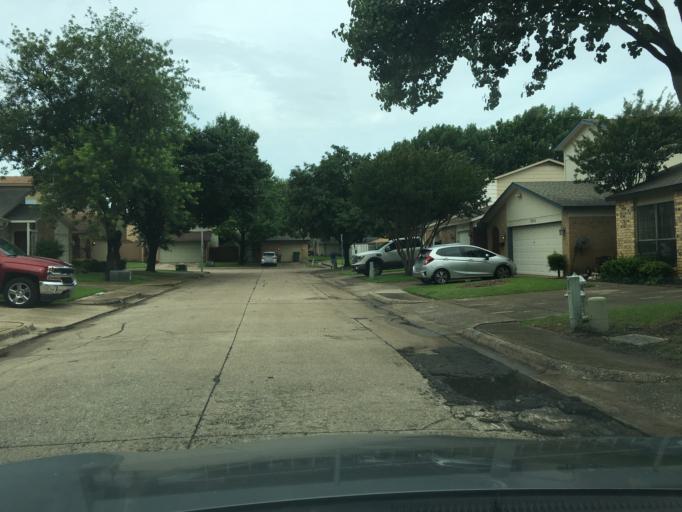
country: US
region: Texas
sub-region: Dallas County
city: Garland
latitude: 32.9497
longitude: -96.6706
